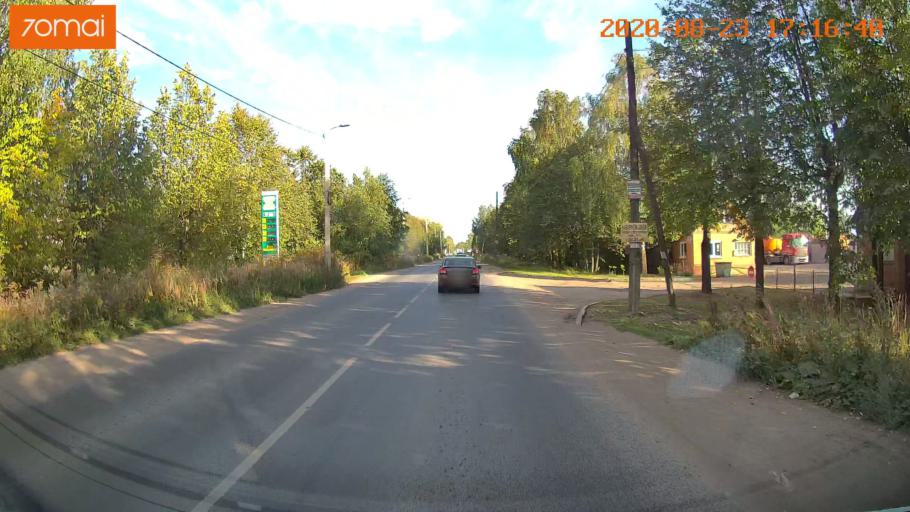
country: RU
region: Ivanovo
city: Novo-Talitsy
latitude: 57.0374
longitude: 40.9125
